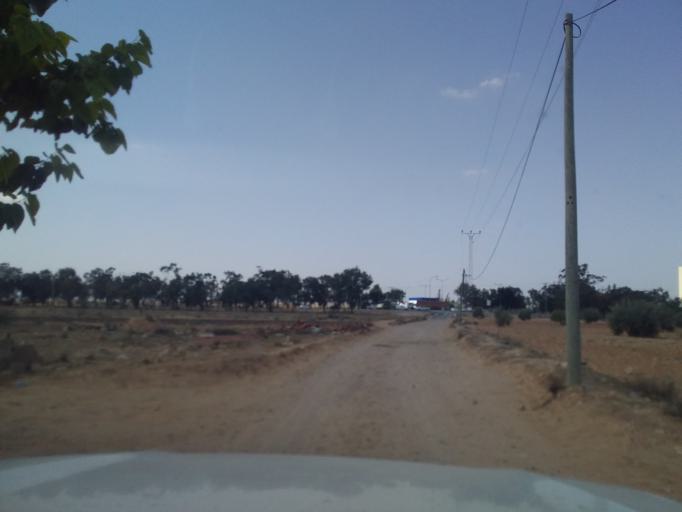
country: TN
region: Madanin
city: Medenine
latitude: 33.5997
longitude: 10.3117
